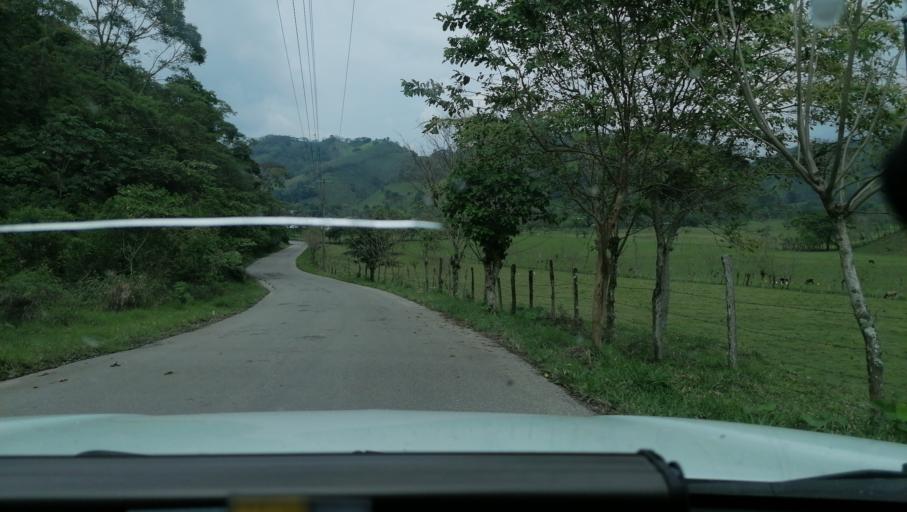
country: MX
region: Chiapas
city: Ixtacomitan
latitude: 17.3309
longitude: -93.1315
